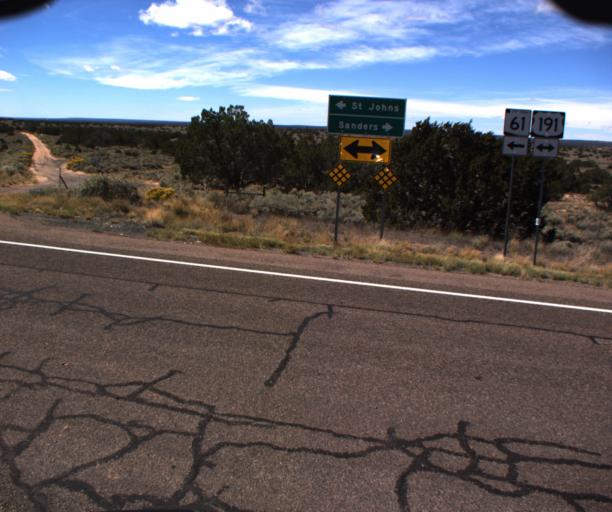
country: US
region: Arizona
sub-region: Apache County
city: Houck
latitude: 34.9024
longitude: -109.2380
